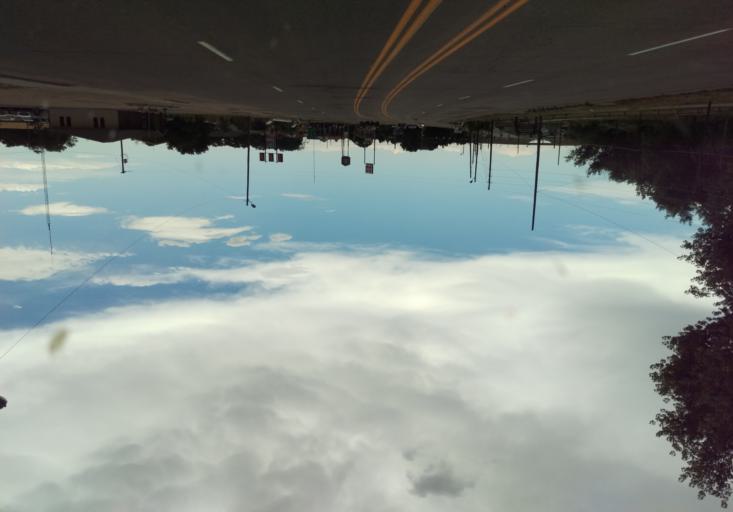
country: US
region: Colorado
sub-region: Logan County
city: Sterling
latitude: 40.6185
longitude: -103.1856
